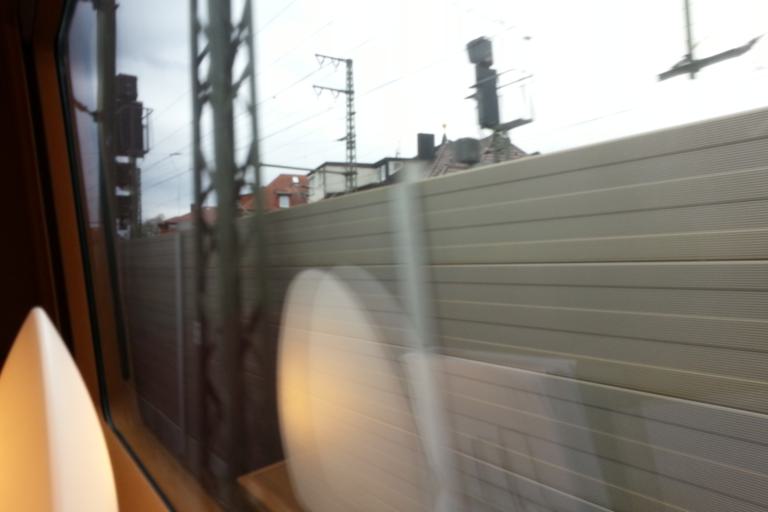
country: DE
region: Thuringia
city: Erfurt
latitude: 50.9680
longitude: 11.0253
